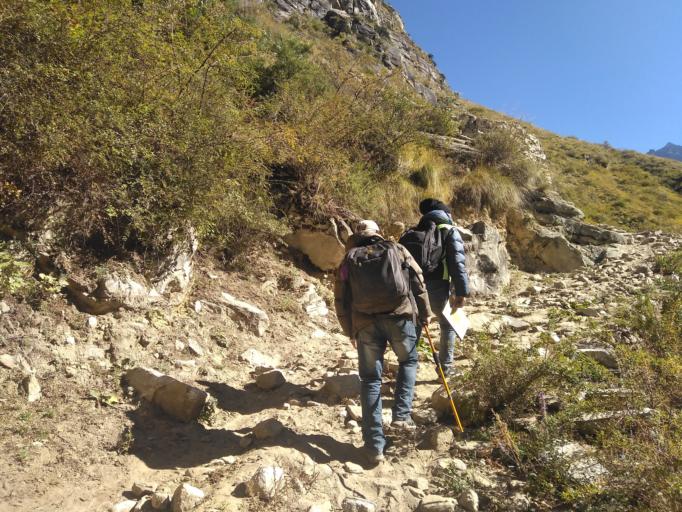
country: NP
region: Western Region
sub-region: Dhawalagiri Zone
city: Jomsom
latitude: 28.9337
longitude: 83.0477
